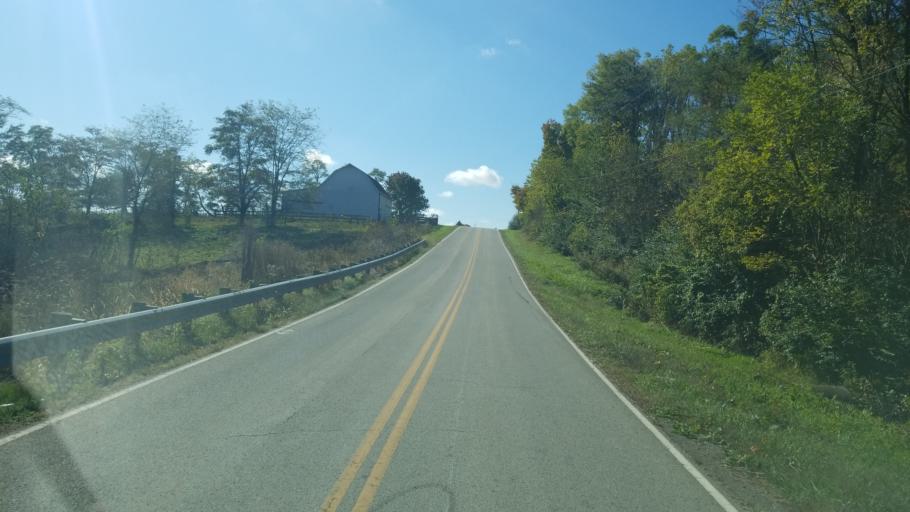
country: US
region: Ohio
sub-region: Highland County
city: Leesburg
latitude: 39.2977
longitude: -83.5794
